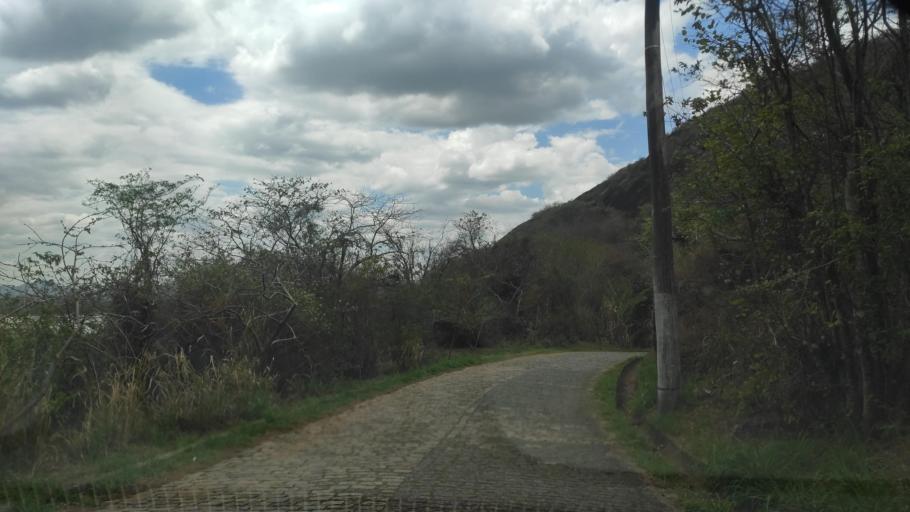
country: BR
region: Espirito Santo
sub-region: Vitoria
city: Vitoria
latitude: -20.2916
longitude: -40.3379
